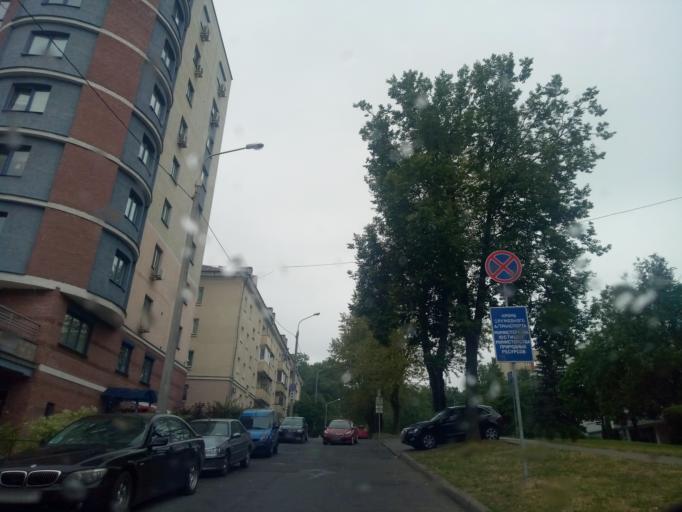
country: BY
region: Minsk
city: Minsk
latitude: 53.9007
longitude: 27.5422
